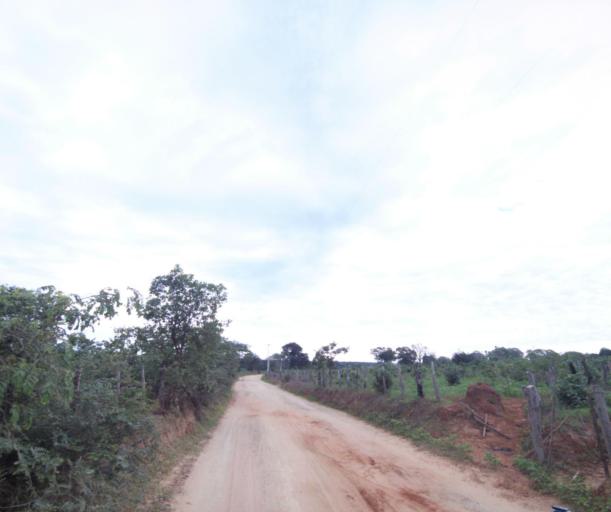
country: BR
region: Bahia
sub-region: Carinhanha
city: Carinhanha
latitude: -14.1804
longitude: -44.5143
